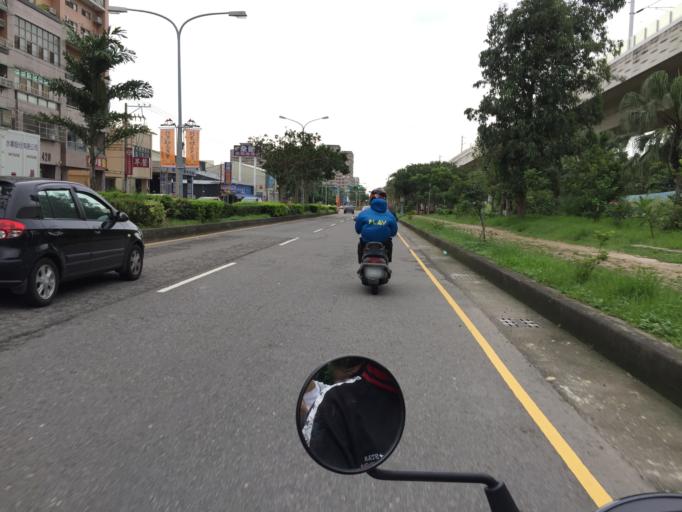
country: TW
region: Taiwan
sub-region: Taichung City
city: Taichung
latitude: 24.1591
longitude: 120.6994
